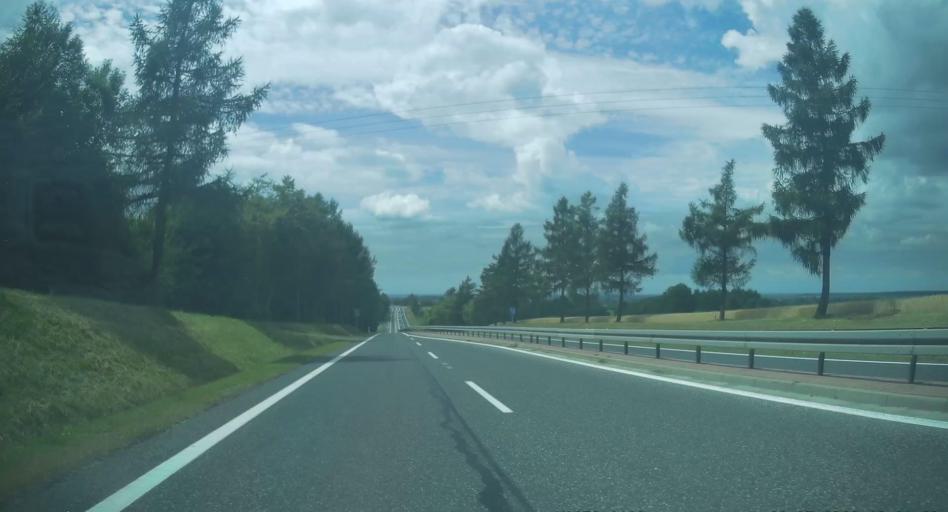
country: PL
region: Subcarpathian Voivodeship
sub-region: Powiat ropczycko-sedziszowski
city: Ropczyce
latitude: 50.0611
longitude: 21.5793
